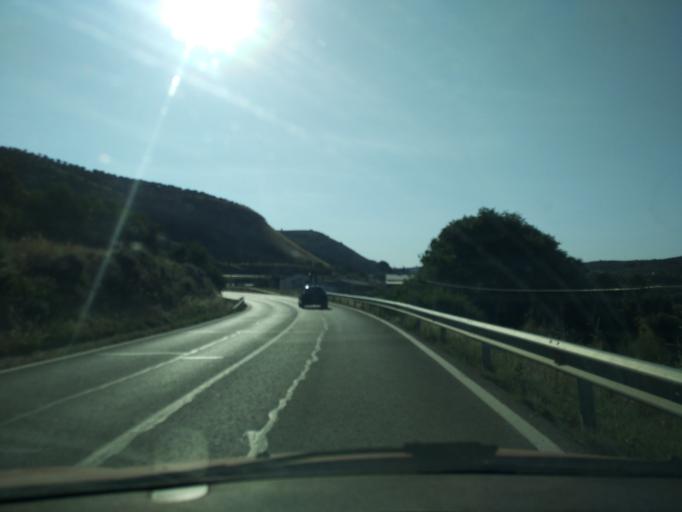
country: ES
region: Madrid
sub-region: Provincia de Madrid
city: Valverde de Alcala
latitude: 40.4176
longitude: -3.3084
